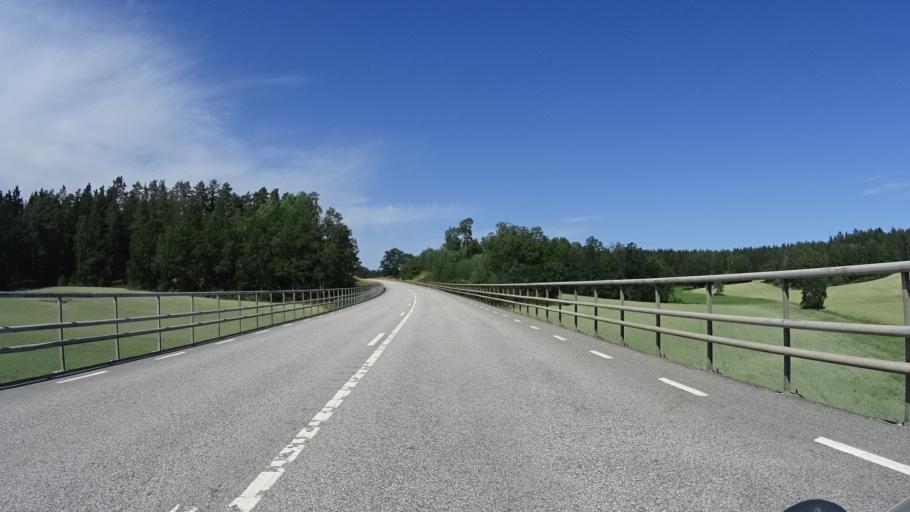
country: SE
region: Kalmar
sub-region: Vasterviks Kommun
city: Gamleby
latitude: 57.9373
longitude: 16.3837
